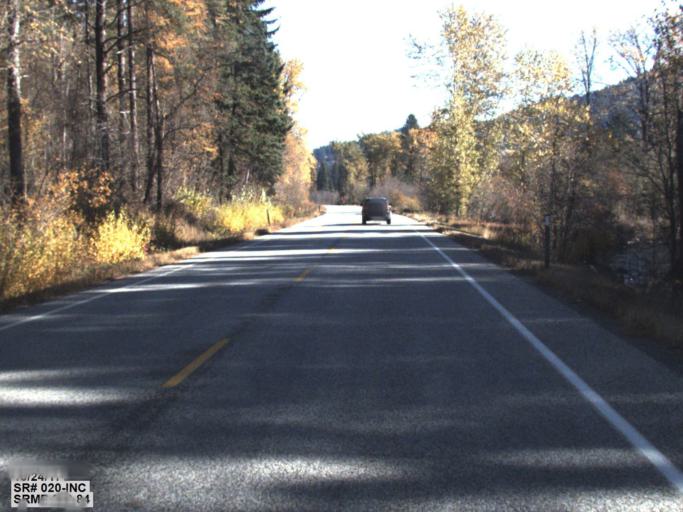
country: US
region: Washington
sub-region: Stevens County
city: Kettle Falls
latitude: 48.5791
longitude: -118.2530
